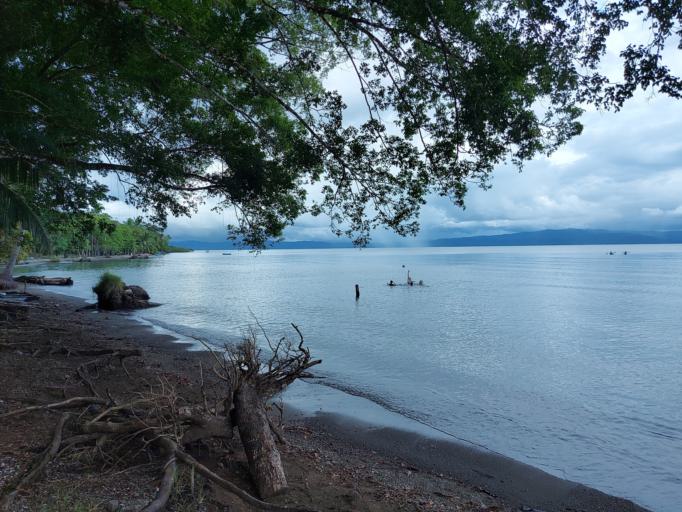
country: CR
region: Puntarenas
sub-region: Canton de Golfito
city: Golfito
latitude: 8.6398
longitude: -83.4356
